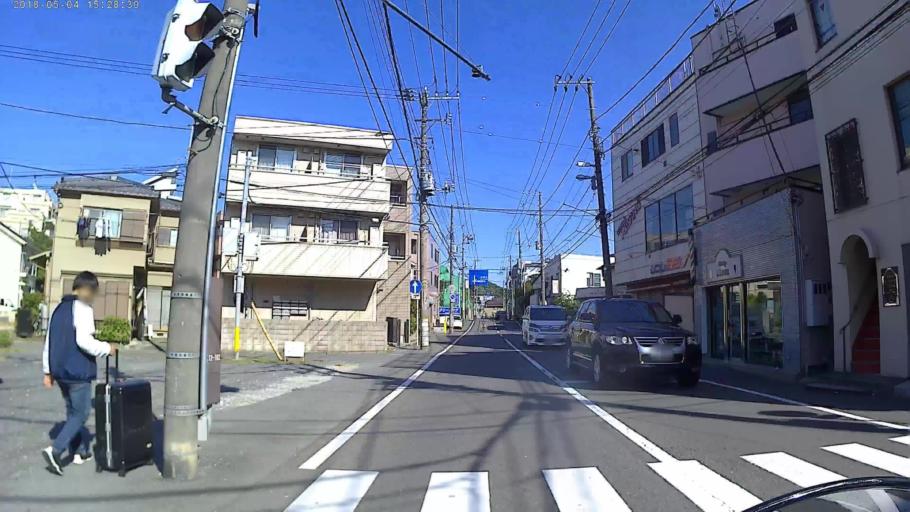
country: JP
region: Kanagawa
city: Yokohama
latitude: 35.5283
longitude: 139.6199
